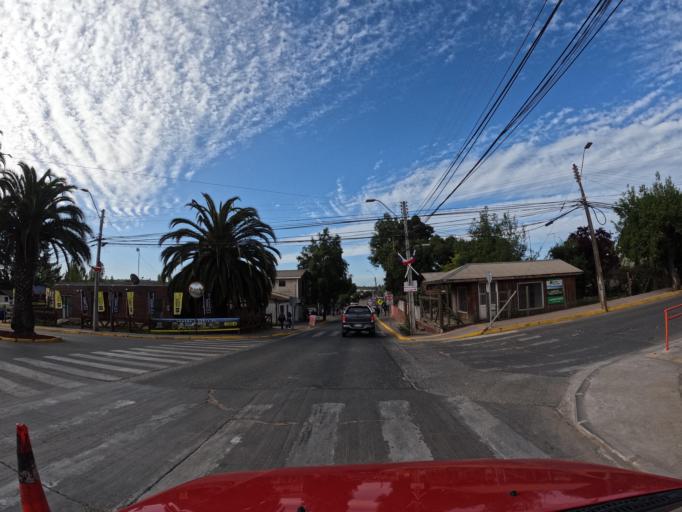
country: CL
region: Valparaiso
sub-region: San Antonio Province
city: San Antonio
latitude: -34.1172
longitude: -71.7269
